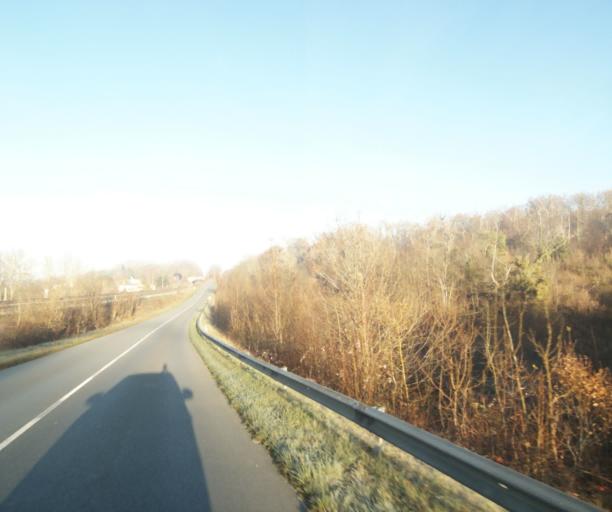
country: FR
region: Poitou-Charentes
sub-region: Departement de la Charente-Maritime
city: Bussac-sur-Charente
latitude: 45.7761
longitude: -0.6243
